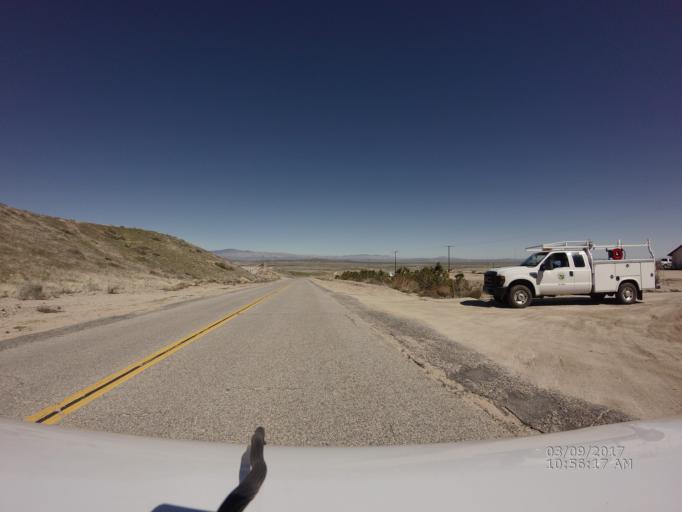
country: US
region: California
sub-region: Los Angeles County
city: Green Valley
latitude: 34.6861
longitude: -118.3849
